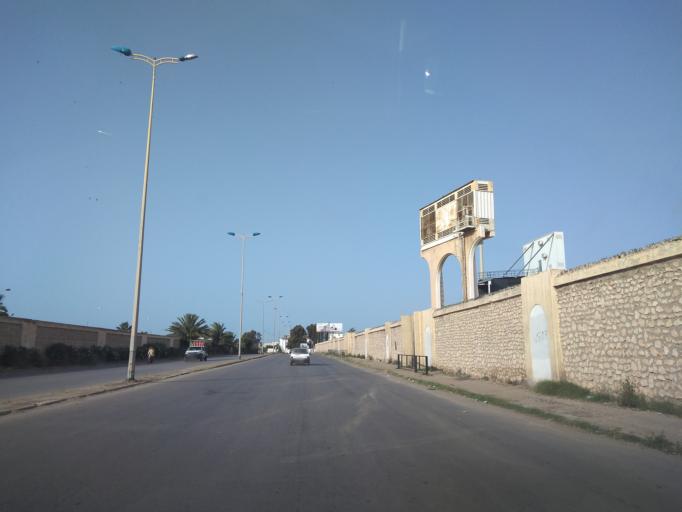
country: TN
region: Safaqis
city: Sfax
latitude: 34.7335
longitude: 10.7479
